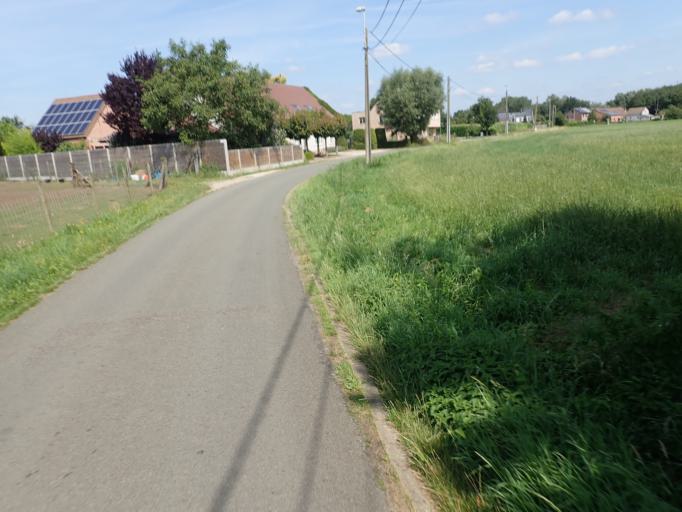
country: BE
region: Flanders
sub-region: Provincie Antwerpen
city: Wommelgem
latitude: 51.2056
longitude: 4.5367
